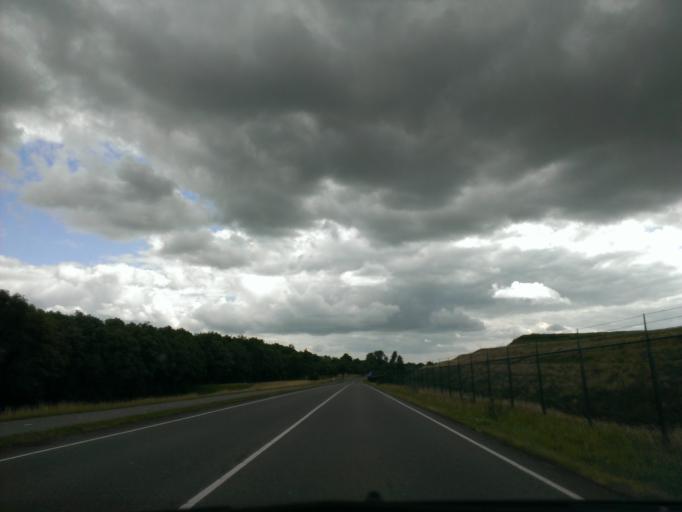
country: NL
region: Gelderland
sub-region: Gemeente Voorst
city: Twello
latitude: 52.2056
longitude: 6.0856
